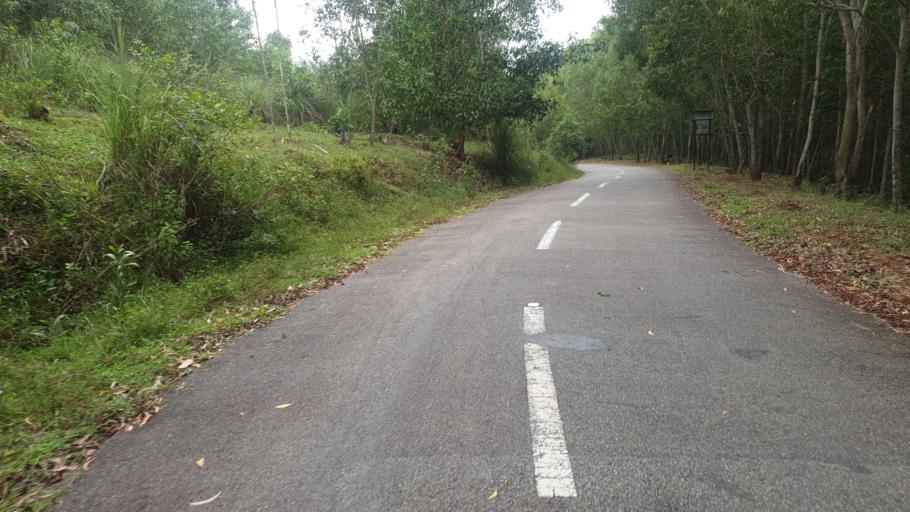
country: IN
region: Kerala
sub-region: Thiruvananthapuram
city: Nedumangad
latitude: 8.6335
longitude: 77.1127
